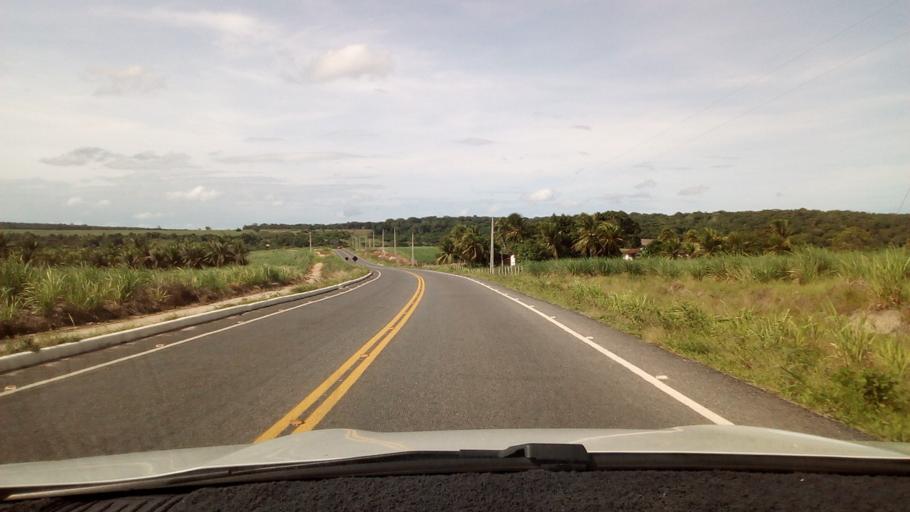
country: BR
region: Paraiba
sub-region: Santa Rita
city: Santa Rita
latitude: -7.0670
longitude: -34.9542
